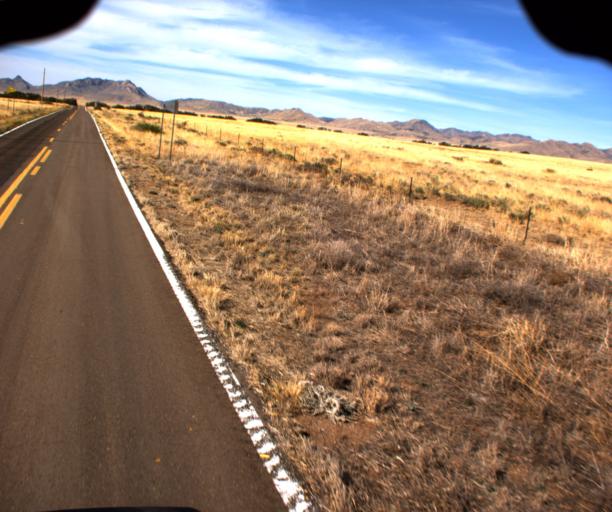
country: US
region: Arizona
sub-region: Cochise County
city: Willcox
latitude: 31.9962
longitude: -109.4400
